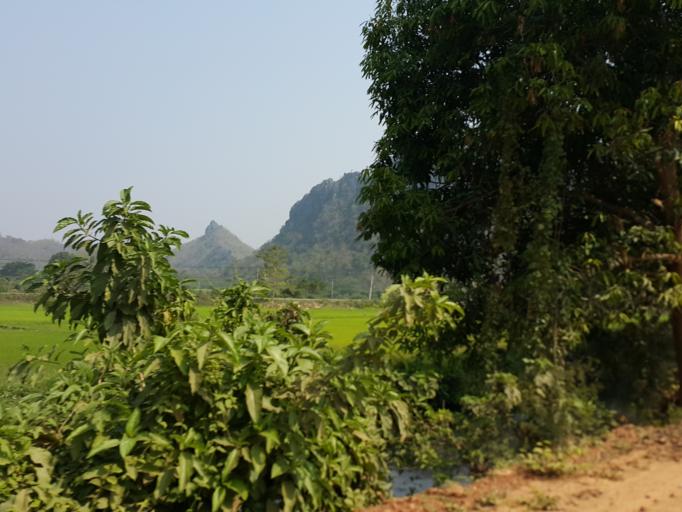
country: TH
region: Sukhothai
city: Thung Saliam
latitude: 17.3301
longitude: 99.4989
